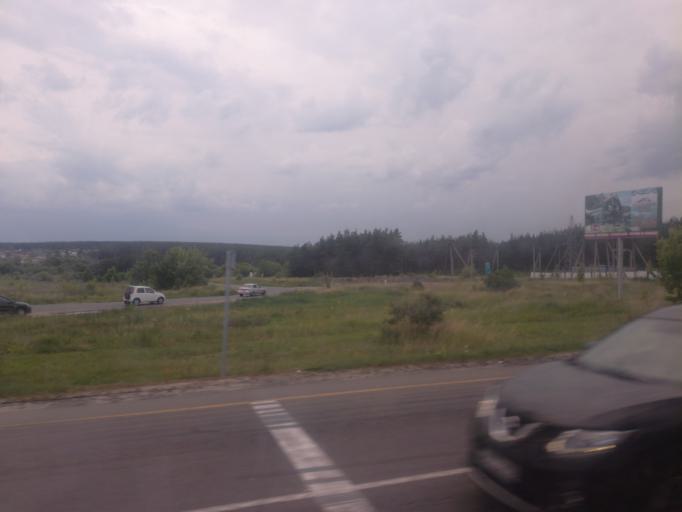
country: RU
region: Kursk
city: Voroshnevo
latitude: 51.7027
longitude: 36.0718
